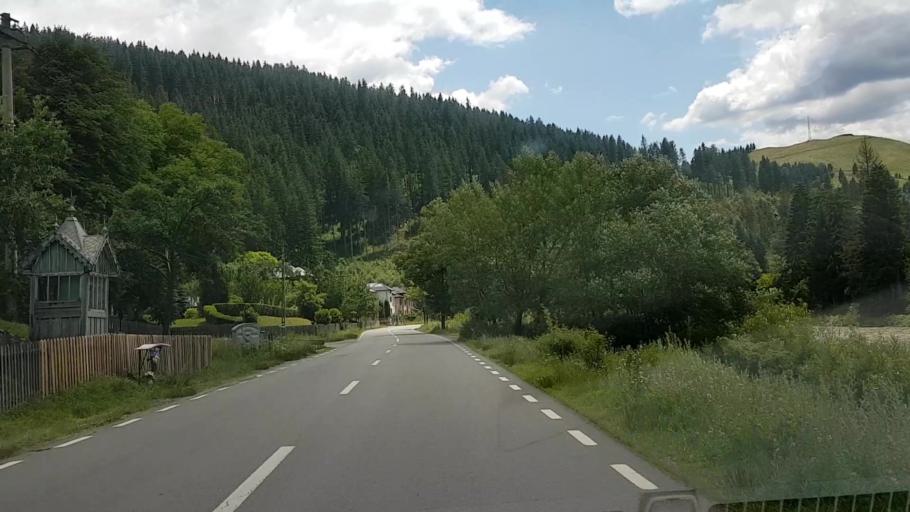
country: RO
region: Suceava
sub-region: Comuna Crucea
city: Crucea
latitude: 47.3562
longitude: 25.6136
